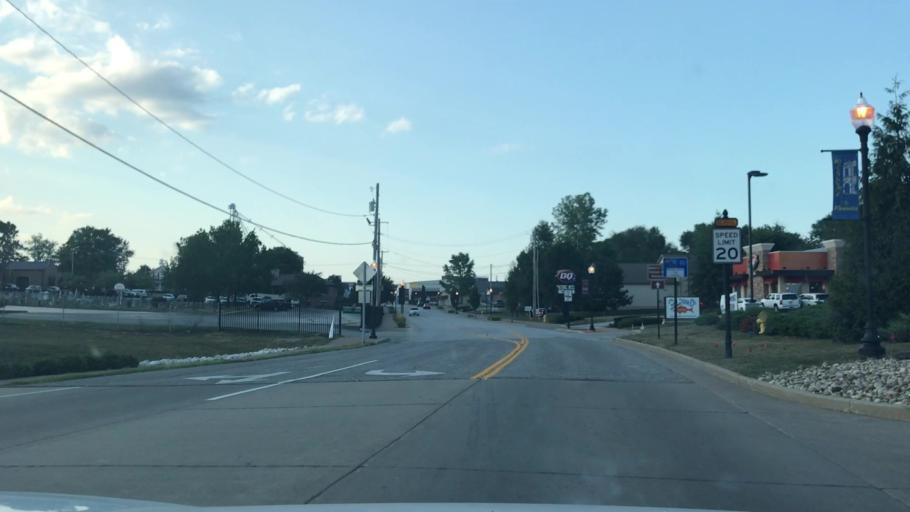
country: US
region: Missouri
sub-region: Saint Charles County
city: Wentzville
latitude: 38.8070
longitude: -90.8542
